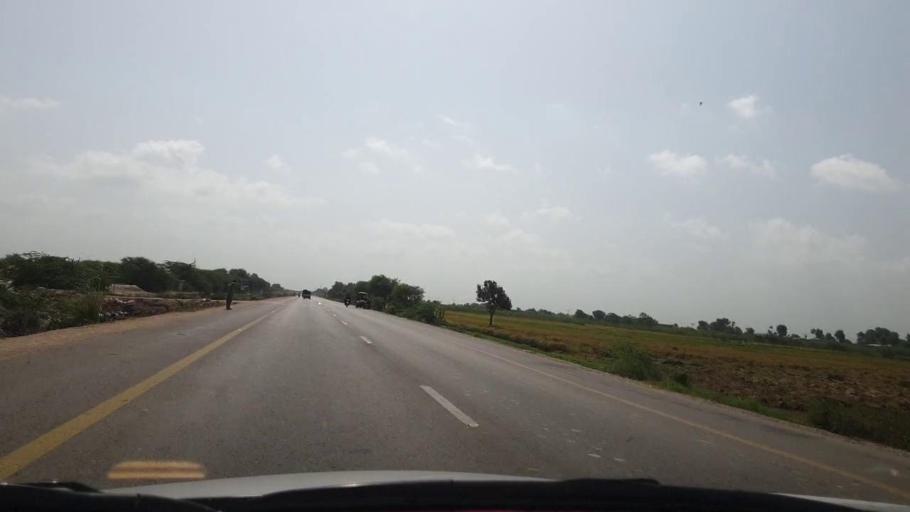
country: PK
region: Sindh
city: Matli
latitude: 24.9793
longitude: 68.6682
